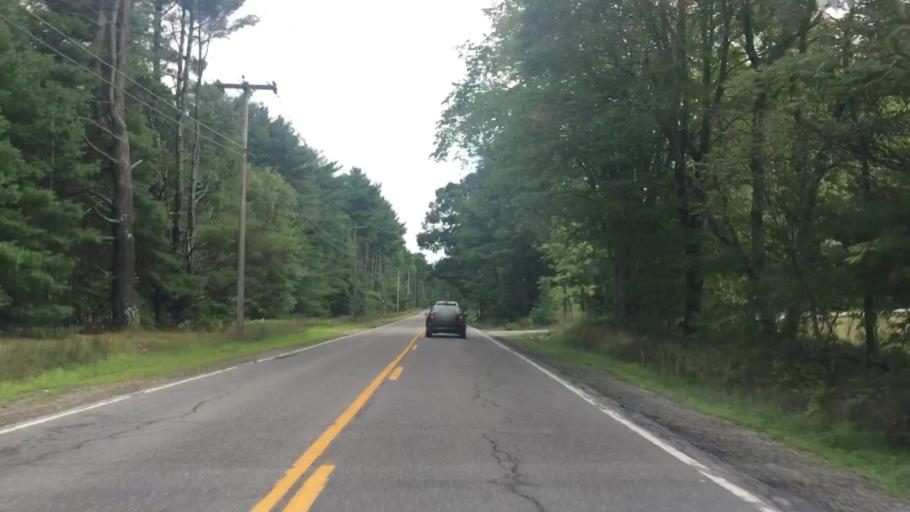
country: US
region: Maine
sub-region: York County
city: Lake Arrowhead
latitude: 43.6123
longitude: -70.7181
